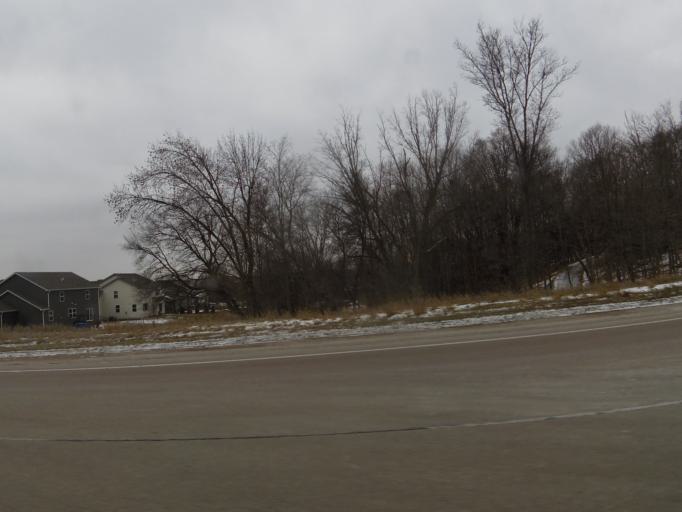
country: US
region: Minnesota
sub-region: Carver County
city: Waconia
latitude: 44.8359
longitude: -93.7694
